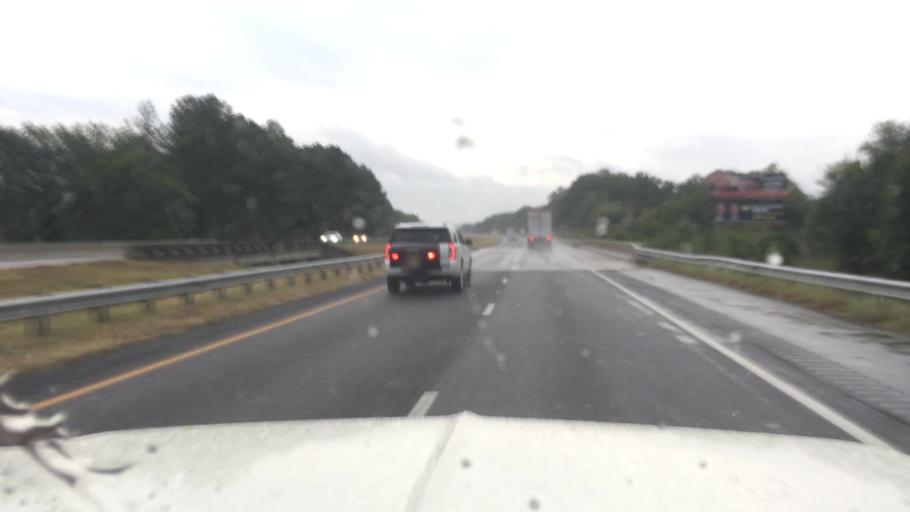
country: US
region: Alabama
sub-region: Morgan County
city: Falkville
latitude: 34.4071
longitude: -86.8983
